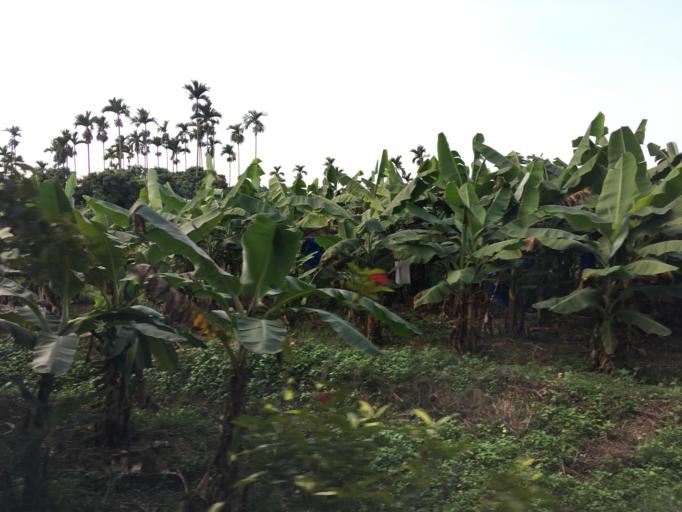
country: TW
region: Taiwan
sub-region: Chiayi
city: Jiayi Shi
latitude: 23.4938
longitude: 120.5220
